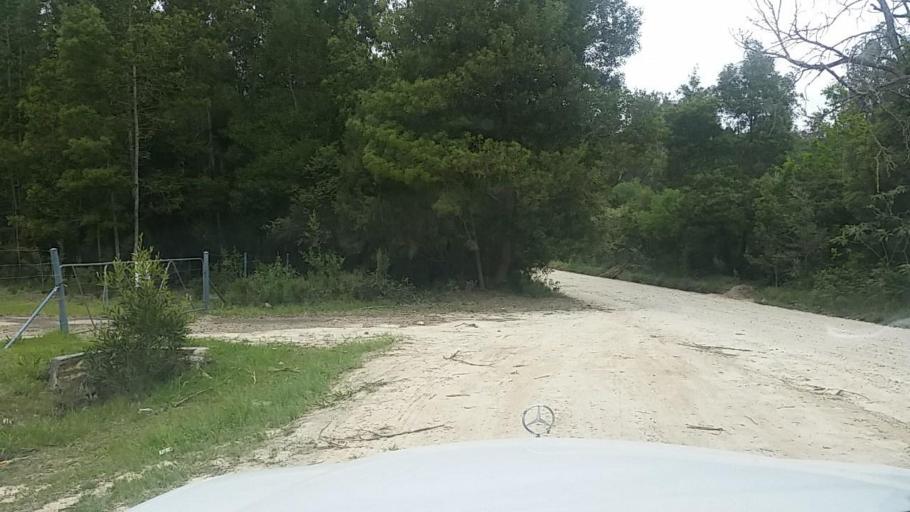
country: ZA
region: Western Cape
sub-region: Eden District Municipality
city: Knysna
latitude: -34.0048
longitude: 23.1185
